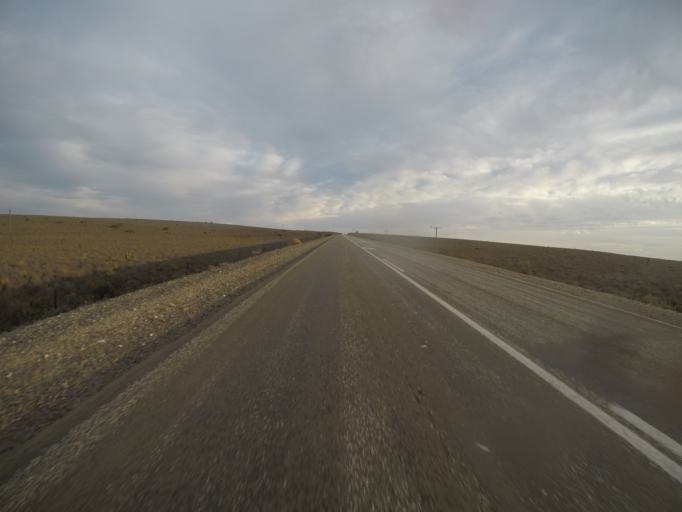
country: ZA
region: Eastern Cape
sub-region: Cacadu District Municipality
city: Willowmore
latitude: -33.5773
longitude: 23.1675
